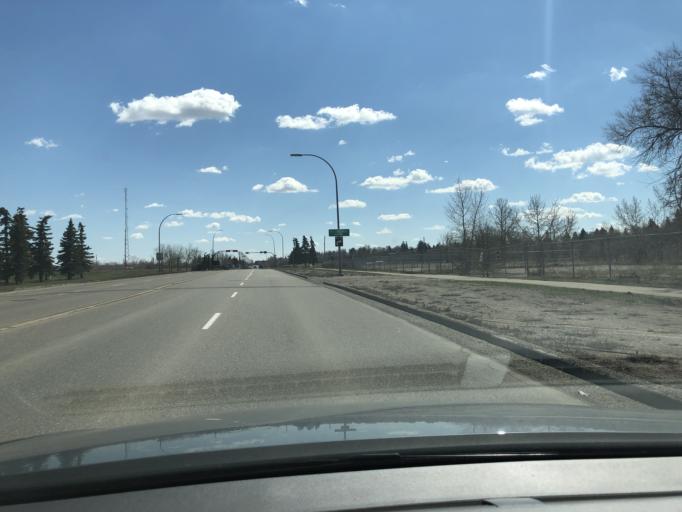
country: CA
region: Alberta
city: Calgary
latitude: 51.0013
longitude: -114.0114
